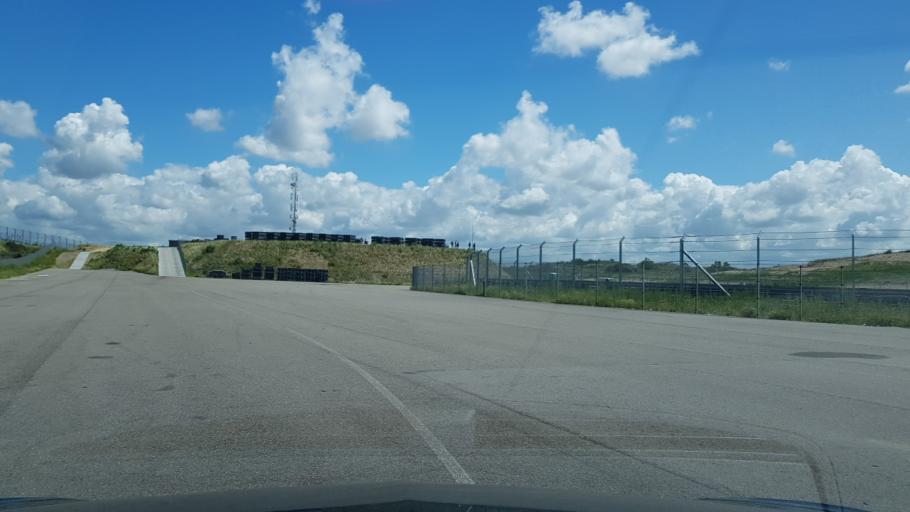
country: NL
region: North Holland
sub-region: Gemeente Zandvoort
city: Zandvoort
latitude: 52.3877
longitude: 4.5415
